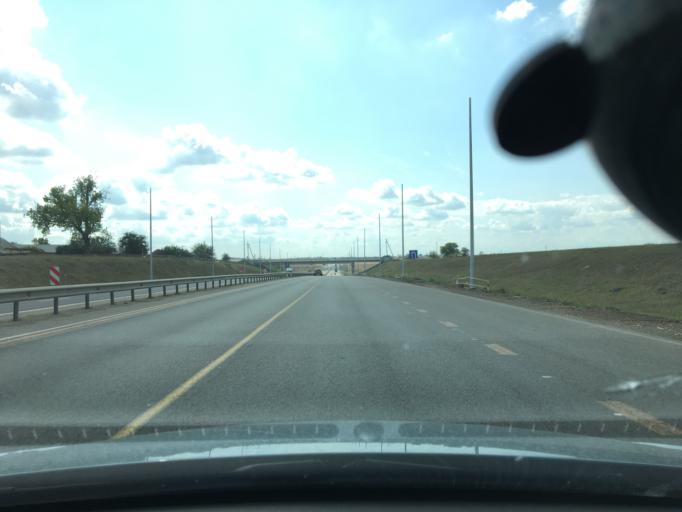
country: RU
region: Krasnodarskiy
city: Berezanskaya
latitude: 45.7369
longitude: 39.6292
